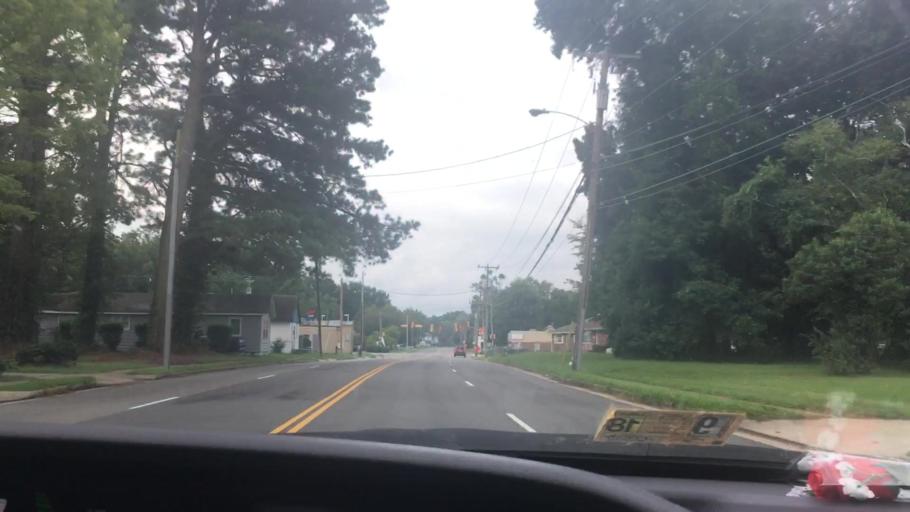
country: US
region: Virginia
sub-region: City of Hampton
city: East Hampton
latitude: 37.0348
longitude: -76.3220
